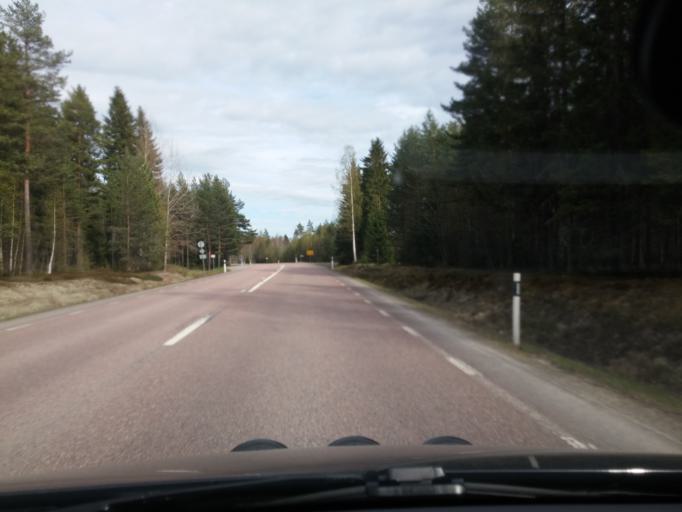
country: SE
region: Gaevleborg
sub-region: Ljusdals Kommun
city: Farila
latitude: 61.8074
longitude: 15.9352
